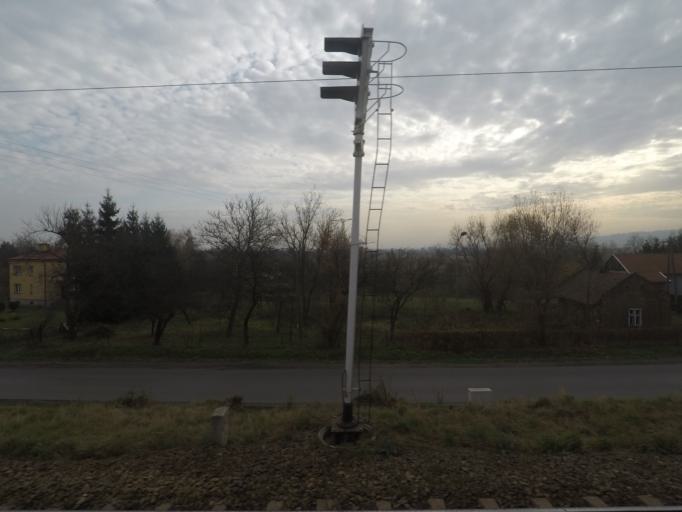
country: PL
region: Subcarpathian Voivodeship
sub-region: Powiat przemyski
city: Zurawica
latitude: 49.8020
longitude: 22.7954
